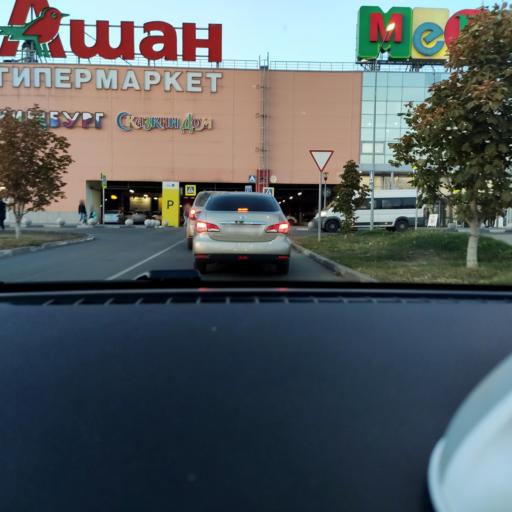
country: RU
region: Samara
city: Petra-Dubrava
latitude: 53.3247
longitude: 50.3052
